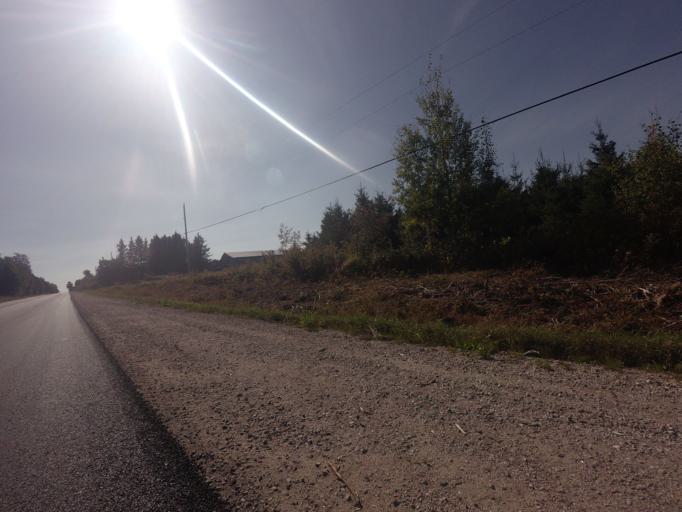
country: CA
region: Quebec
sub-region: Outaouais
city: Maniwaki
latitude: 46.5417
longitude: -75.8238
